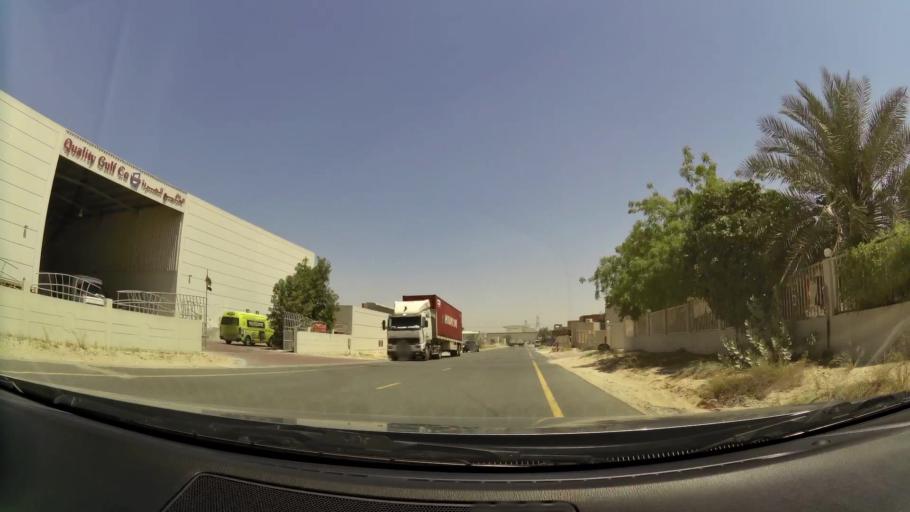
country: AE
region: Dubai
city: Dubai
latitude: 24.9840
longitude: 55.1876
